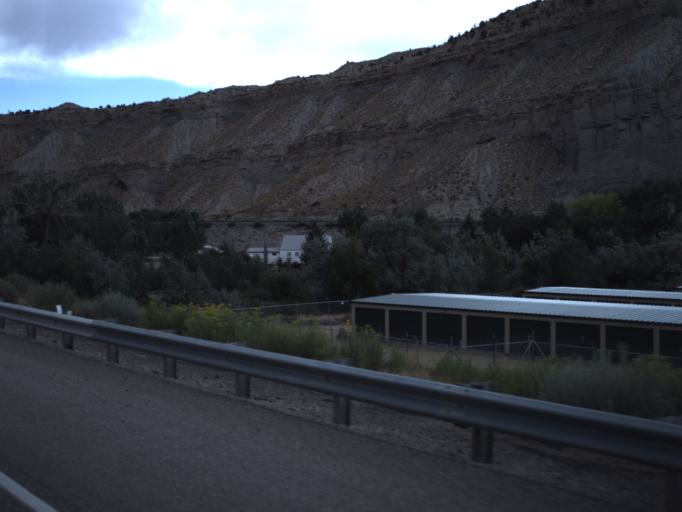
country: US
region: Utah
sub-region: Carbon County
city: Spring Glen
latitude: 39.6385
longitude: -110.8600
